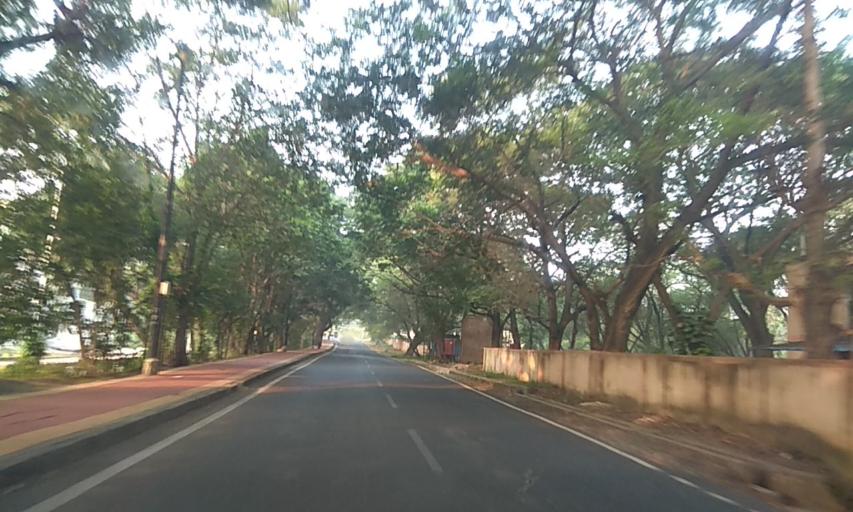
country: IN
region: Maharashtra
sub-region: Pune Division
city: Khadki
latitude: 18.5572
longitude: 73.8569
